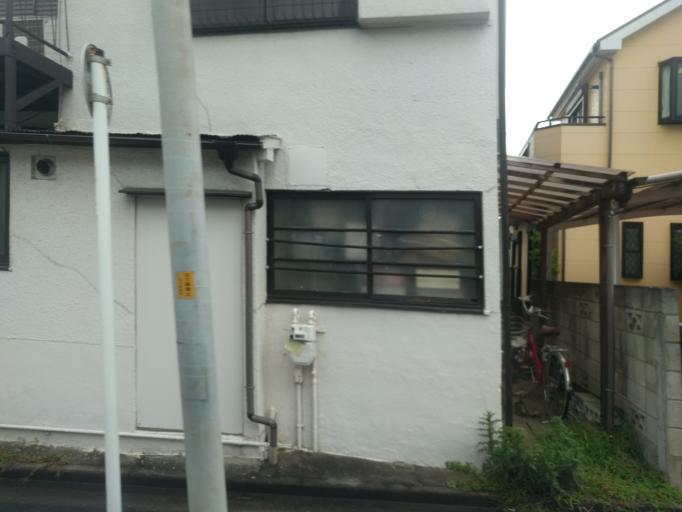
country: JP
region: Saitama
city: Shimotoda
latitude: 35.8320
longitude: 139.6769
